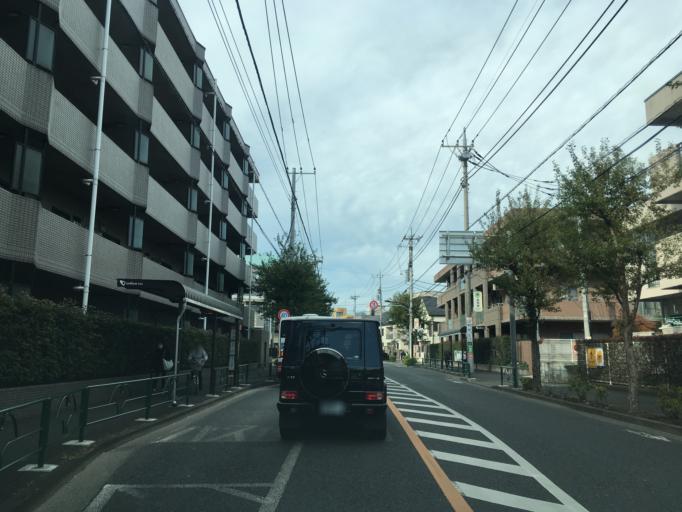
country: JP
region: Tokyo
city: Chofugaoka
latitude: 35.6383
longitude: 139.5739
